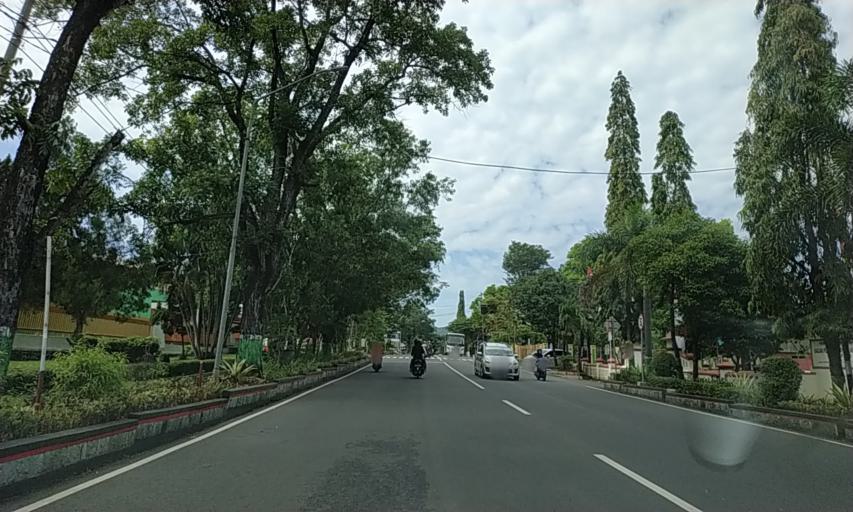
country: ID
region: Central Java
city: Selogiri
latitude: -7.7947
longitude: 110.9052
